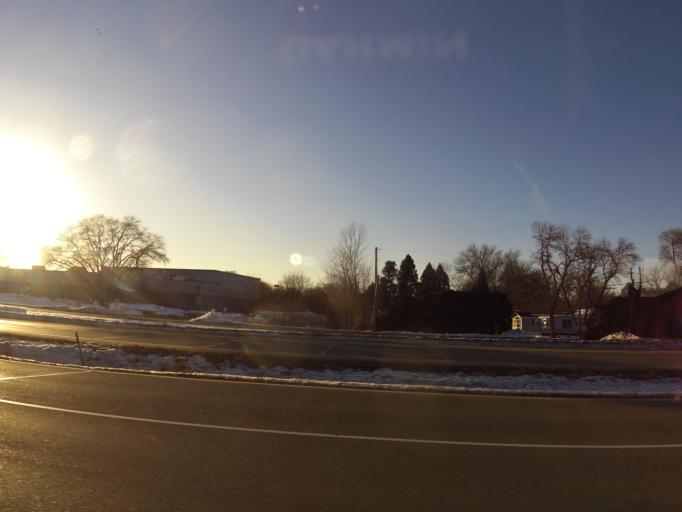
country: US
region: Minnesota
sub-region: Ramsey County
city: Little Canada
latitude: 45.0176
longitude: -93.0520
